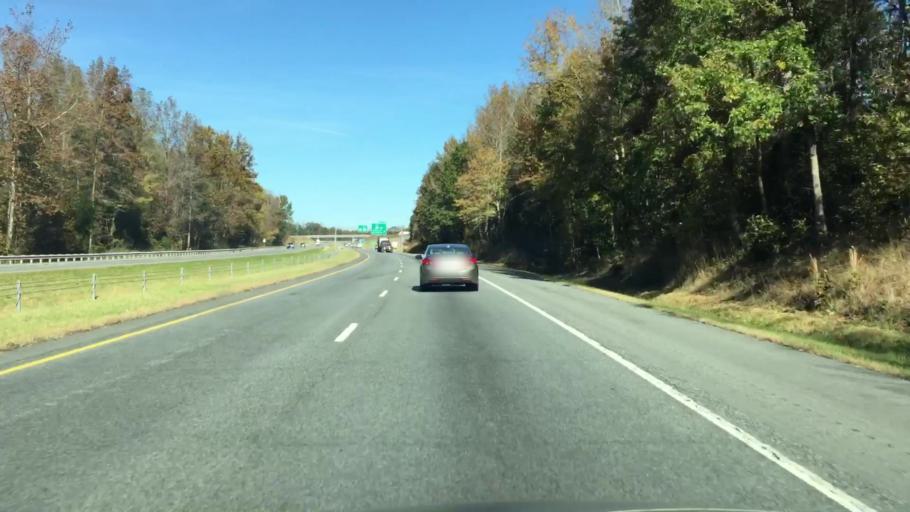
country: US
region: North Carolina
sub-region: Rockingham County
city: Reidsville
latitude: 36.3030
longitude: -79.6415
